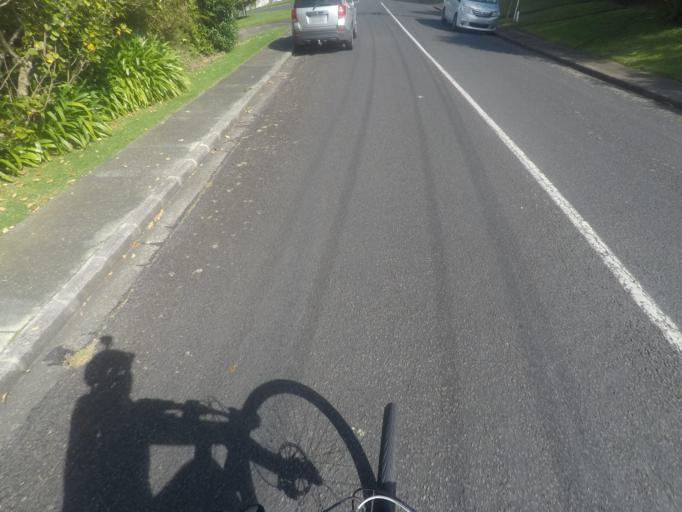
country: NZ
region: Auckland
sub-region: Auckland
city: Mangere
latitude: -36.9244
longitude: 174.7677
